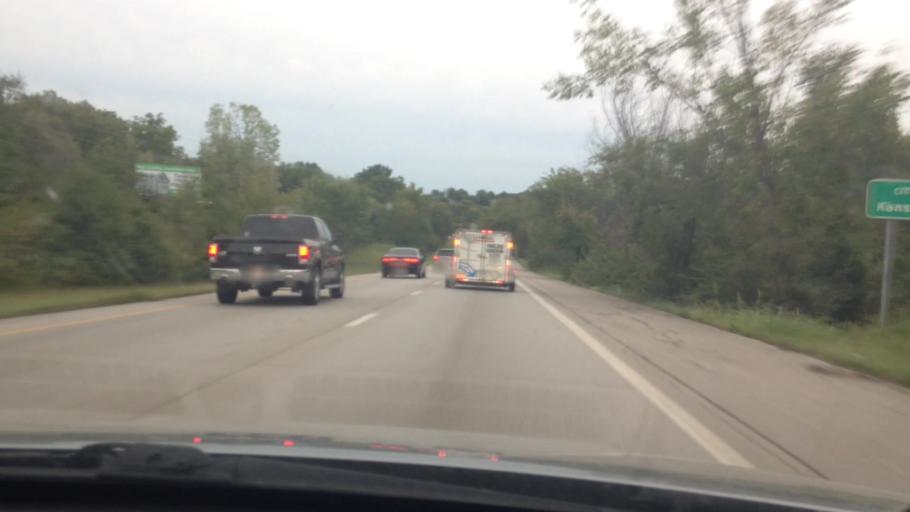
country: US
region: Missouri
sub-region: Jackson County
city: Raytown
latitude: 38.9710
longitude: -94.4417
